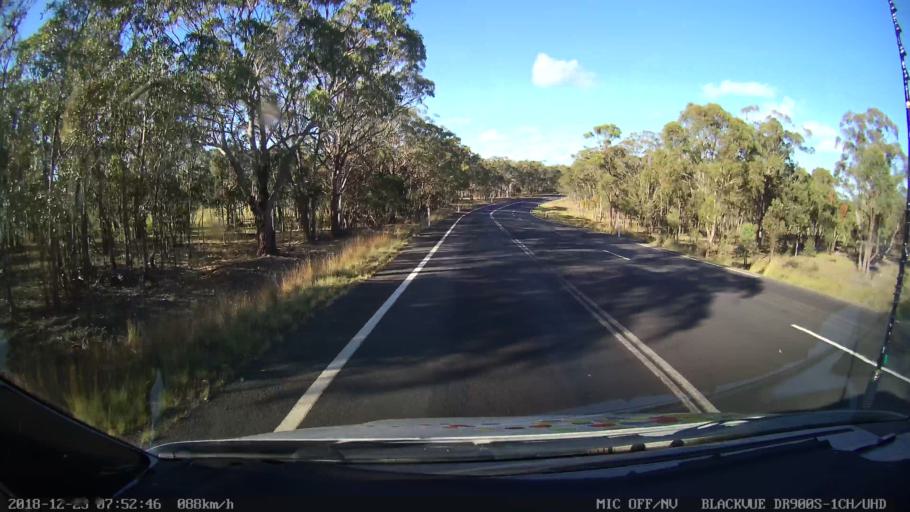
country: AU
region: New South Wales
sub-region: Armidale Dumaresq
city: Armidale
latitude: -30.5317
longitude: 151.8168
